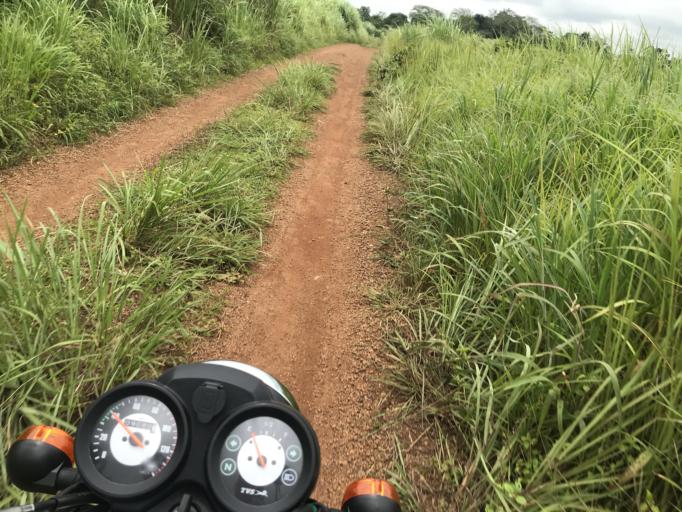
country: SL
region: Eastern Province
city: Buedu
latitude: 8.4717
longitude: -10.3185
